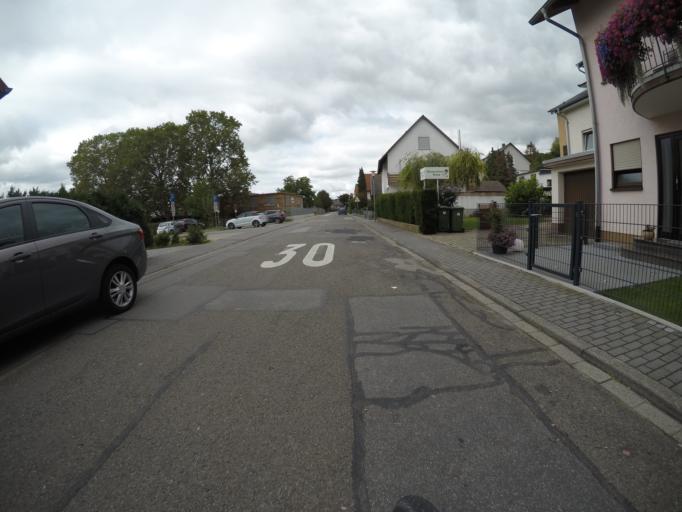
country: DE
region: Baden-Wuerttemberg
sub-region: Karlsruhe Region
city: Laudenbach
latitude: 49.6124
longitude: 8.6528
